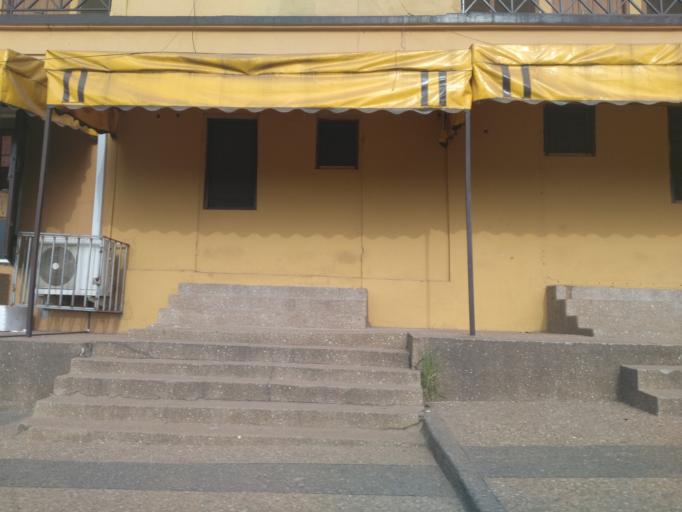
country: GH
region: Ashanti
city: Kumasi
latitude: 6.6872
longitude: -1.6144
